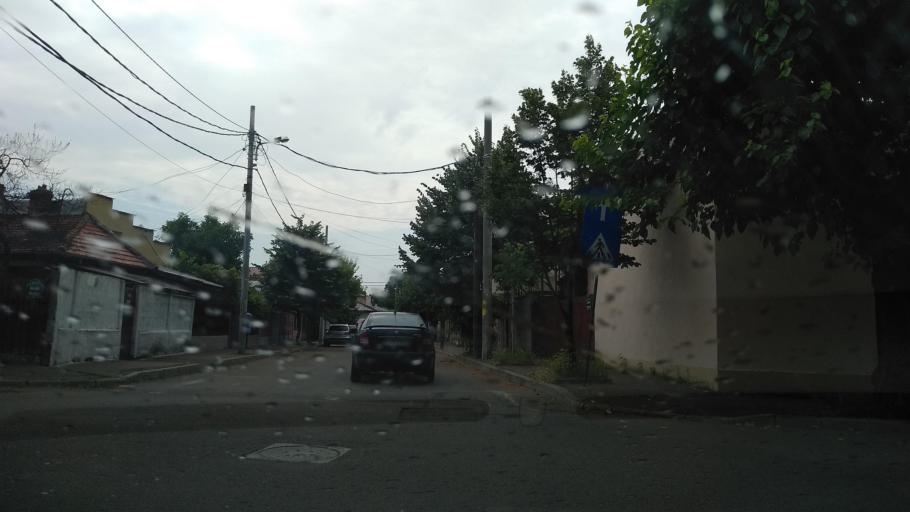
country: RO
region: Ilfov
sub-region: Comuna Fundeni-Dobroesti
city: Fundeni
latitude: 44.4582
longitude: 26.1414
